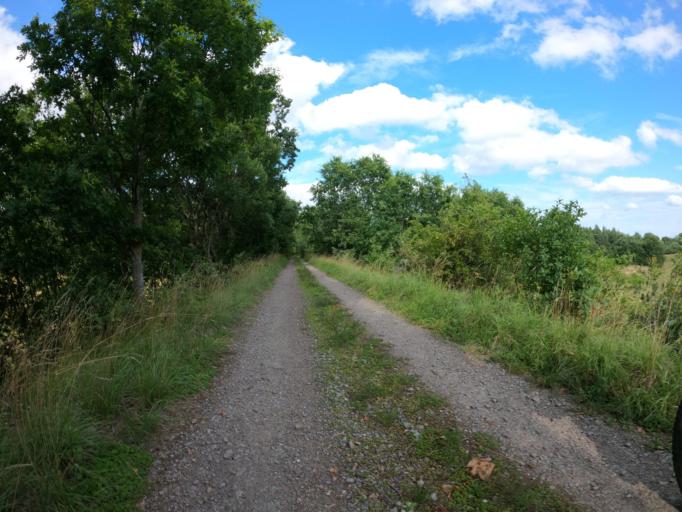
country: PL
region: West Pomeranian Voivodeship
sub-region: Powiat szczecinecki
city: Grzmiaca
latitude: 53.8684
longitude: 16.4516
